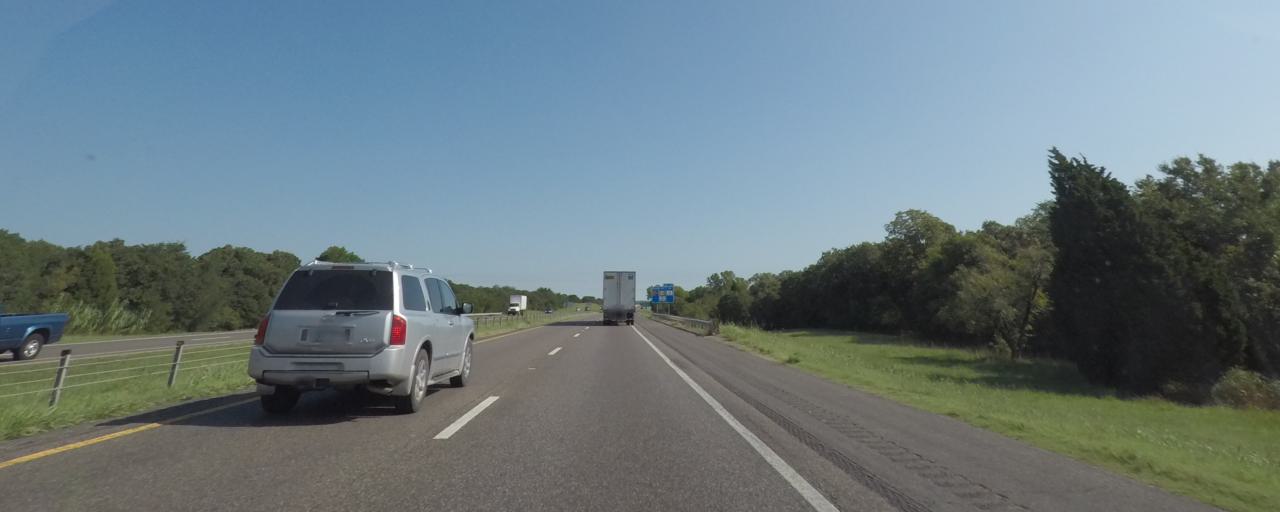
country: US
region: Oklahoma
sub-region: Oklahoma County
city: Edmond
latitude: 35.6695
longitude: -97.4208
